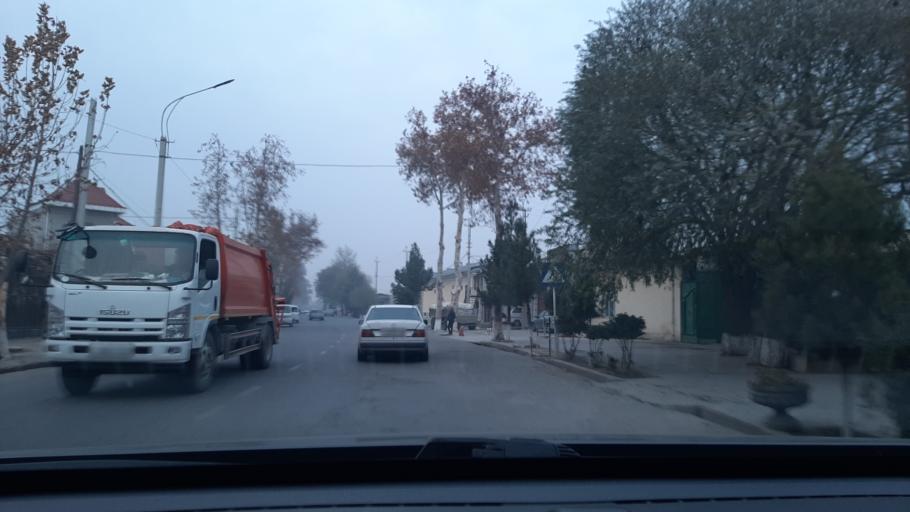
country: TJ
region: Viloyati Sughd
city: Khujand
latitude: 40.2619
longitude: 69.5986
